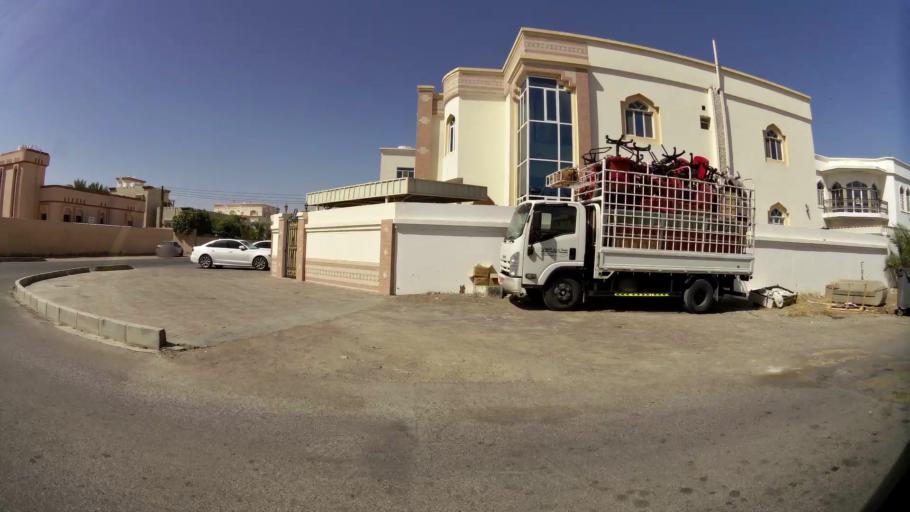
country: OM
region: Muhafazat Masqat
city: As Sib al Jadidah
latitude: 23.6079
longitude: 58.2403
